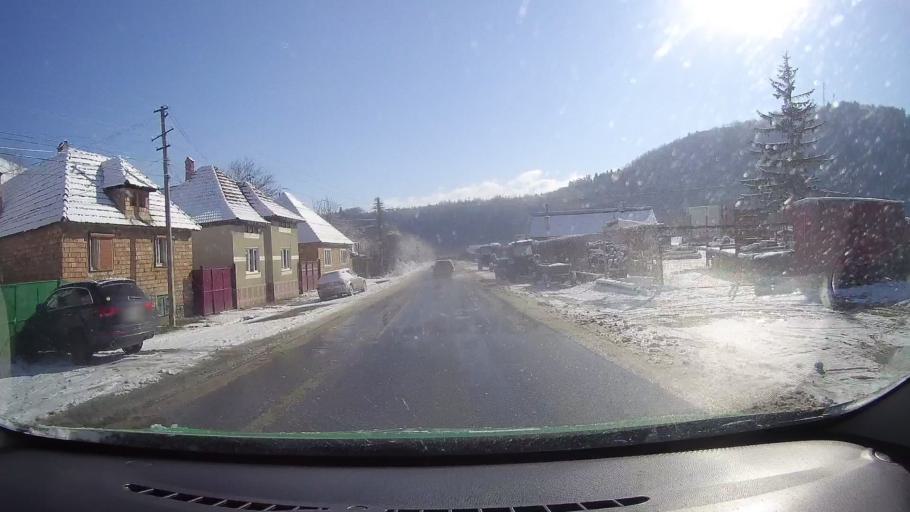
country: RO
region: Sibiu
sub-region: Comuna Talmaciu
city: Talmaciu
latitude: 45.6581
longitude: 24.2685
